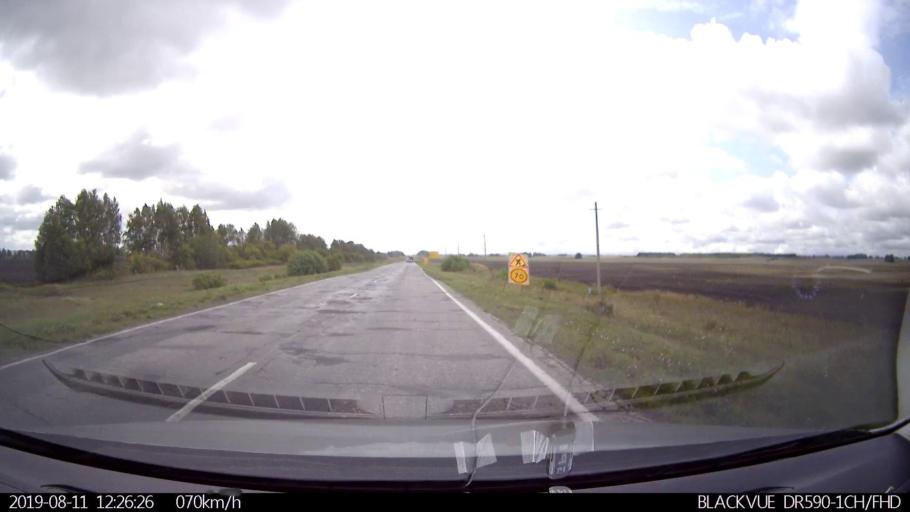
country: RU
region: Ulyanovsk
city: Ignatovka
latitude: 53.8640
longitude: 47.9304
